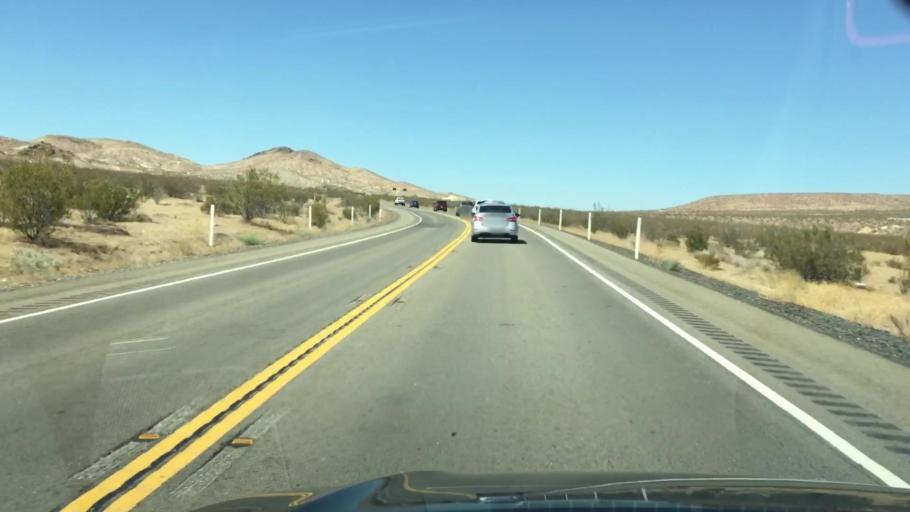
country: US
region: California
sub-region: Kern County
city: Ridgecrest
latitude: 35.3351
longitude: -117.6187
